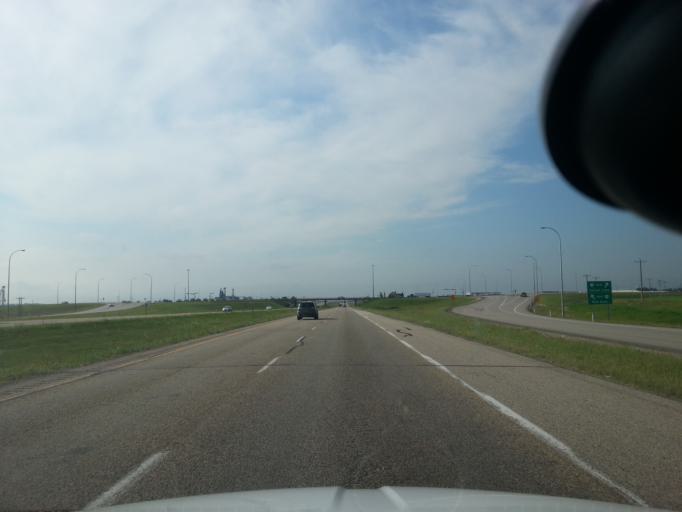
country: CA
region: Alberta
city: Red Deer
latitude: 52.3222
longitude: -113.8614
